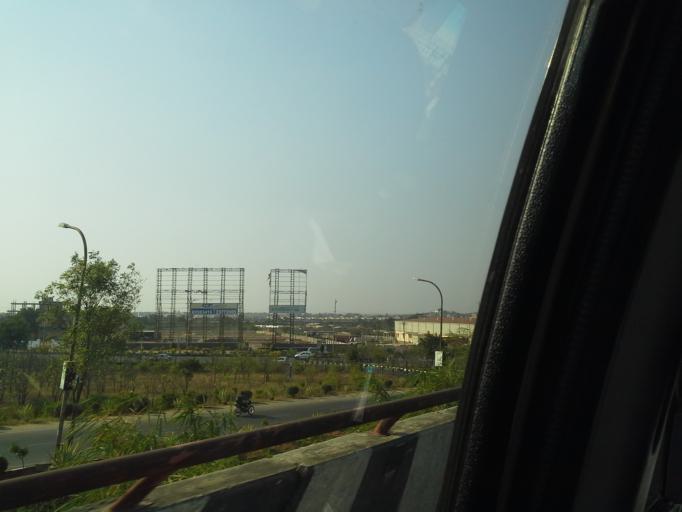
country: IN
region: Telangana
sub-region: Rangareddi
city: Sriramnagar
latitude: 17.2542
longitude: 78.3819
